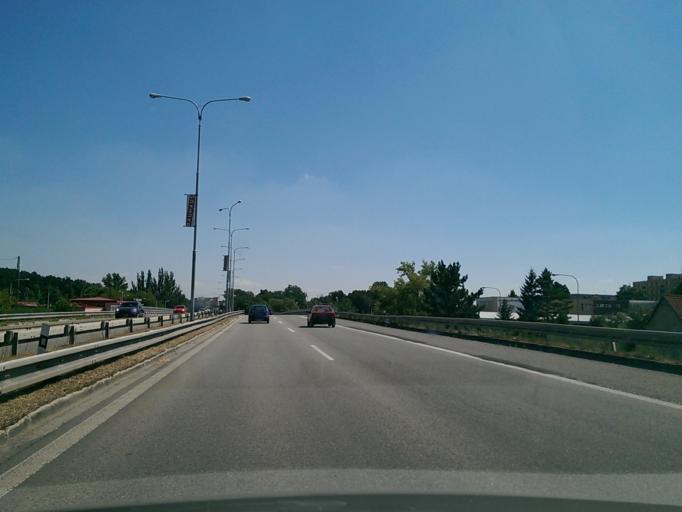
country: CZ
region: South Moravian
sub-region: Mesto Brno
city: Mokra Hora
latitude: 49.2321
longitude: 16.5940
